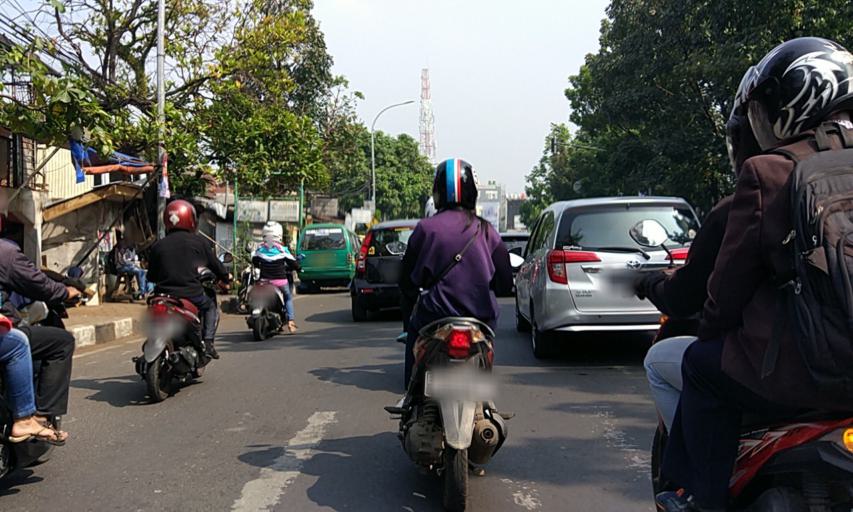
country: ID
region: West Java
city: Bandung
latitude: -6.8982
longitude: 107.6358
